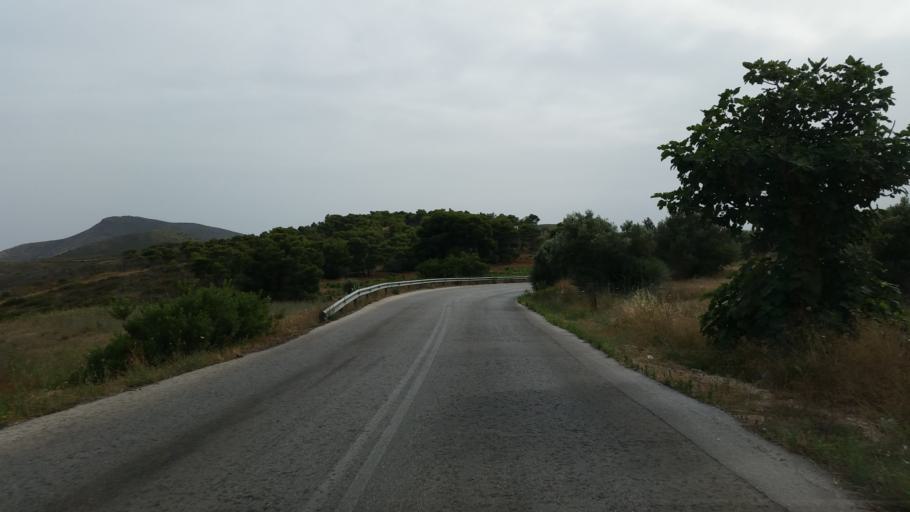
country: GR
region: Attica
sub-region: Nomarchia Anatolikis Attikis
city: Palaia Fokaia
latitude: 37.7205
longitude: 24.0019
